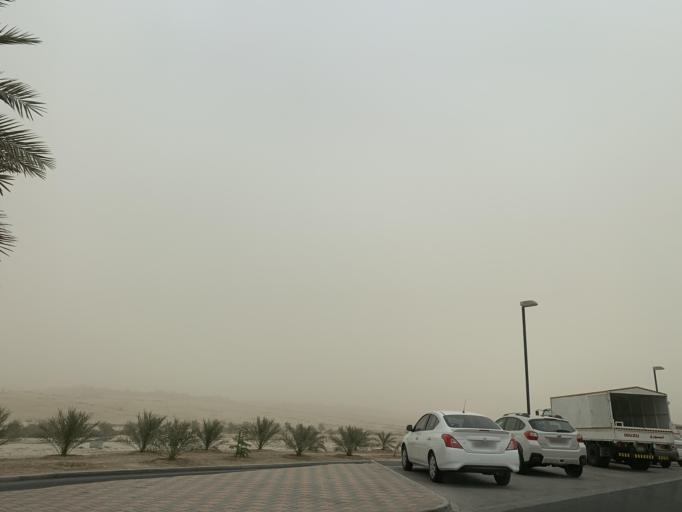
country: BH
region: Central Governorate
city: Madinat Hamad
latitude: 26.1318
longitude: 50.5133
